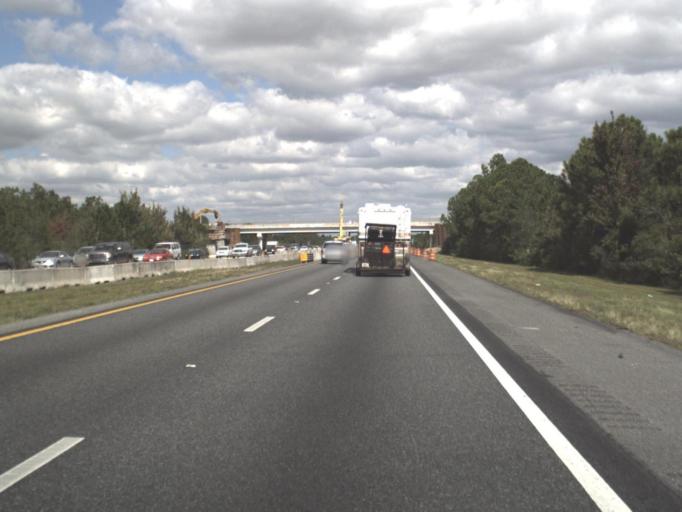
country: US
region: Florida
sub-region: Orange County
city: Southchase
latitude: 28.3886
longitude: -81.3911
